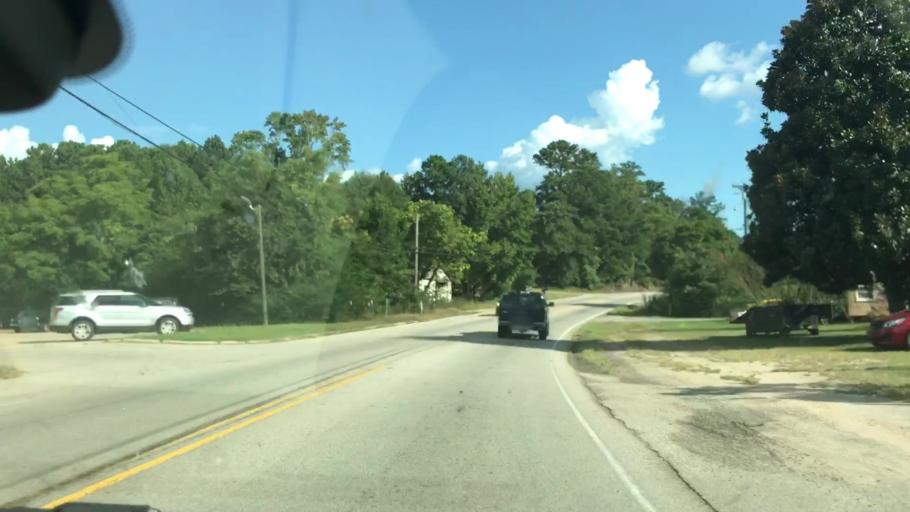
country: US
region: Georgia
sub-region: Troup County
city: La Grange
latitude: 32.9812
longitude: -84.9929
